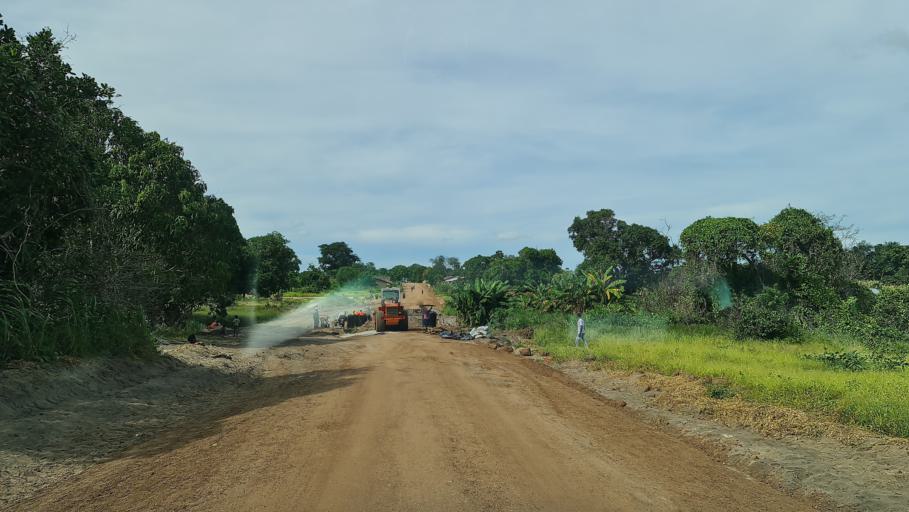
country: MZ
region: Nampula
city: Ilha de Mocambique
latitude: -14.8850
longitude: 40.4742
